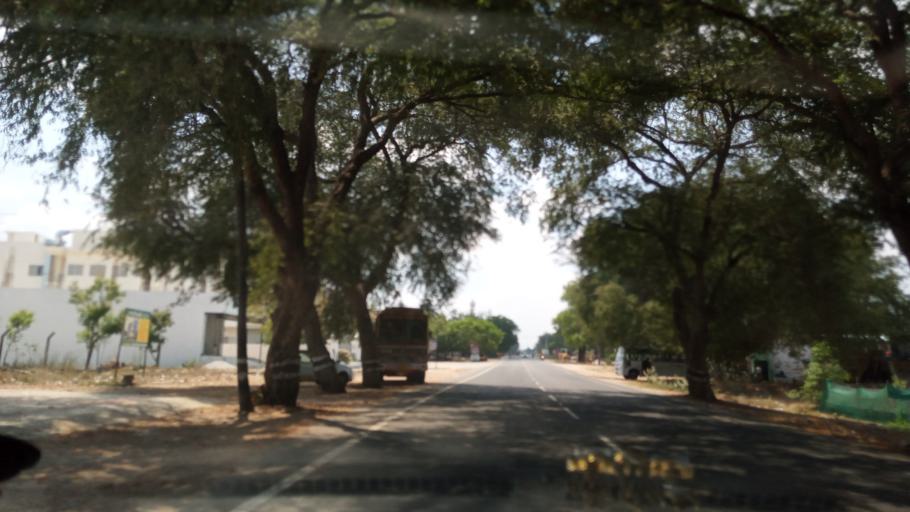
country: IN
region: Tamil Nadu
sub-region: Vellore
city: Walajapet
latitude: 12.9202
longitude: 79.3803
